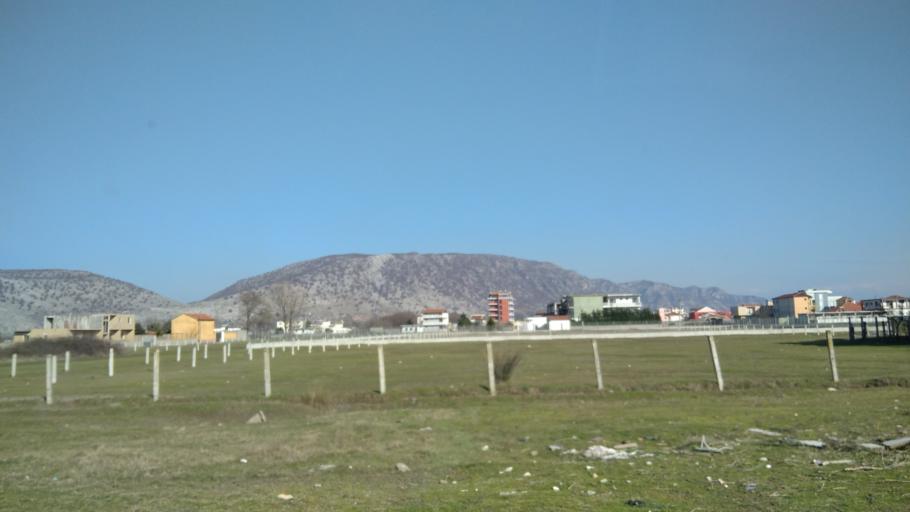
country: AL
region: Shkoder
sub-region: Rrethi i Shkodres
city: Velipoje
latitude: 41.8689
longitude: 19.4213
